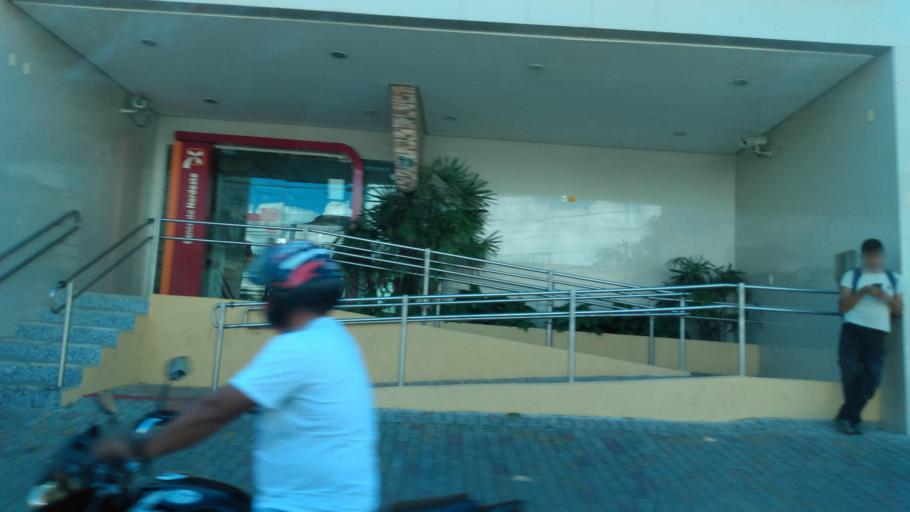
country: BR
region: Pernambuco
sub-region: Gravata
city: Gravata
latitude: -8.2012
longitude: -35.5659
